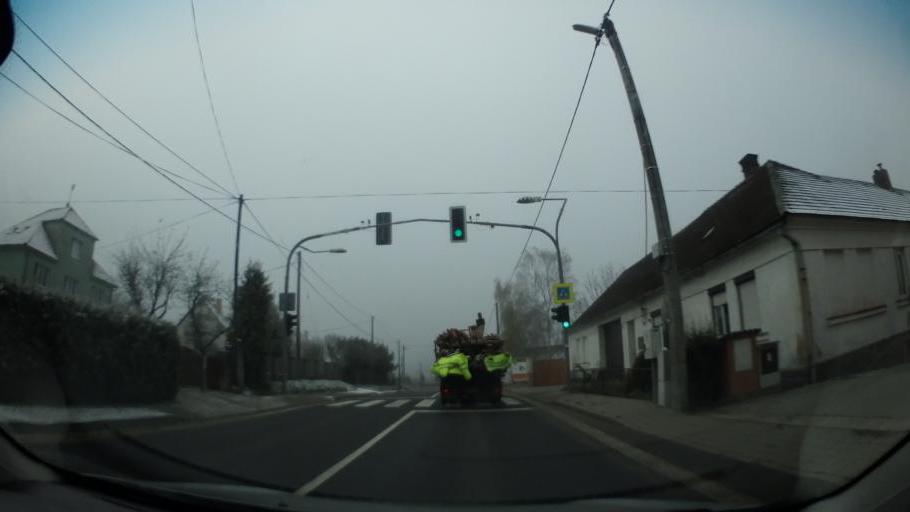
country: CZ
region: Vysocina
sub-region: Okres Trebic
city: Trebic
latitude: 49.2418
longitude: 15.8978
